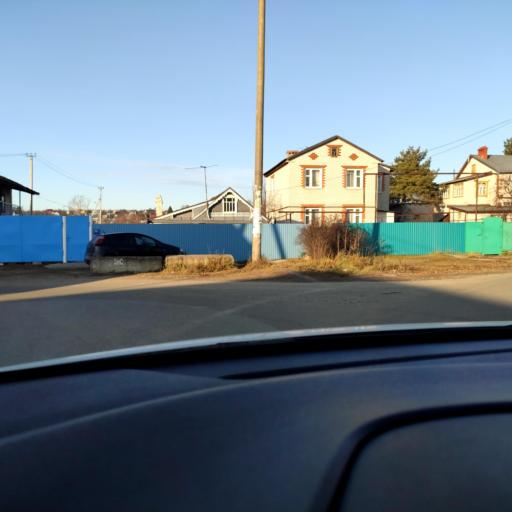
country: RU
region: Tatarstan
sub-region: Gorod Kazan'
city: Kazan
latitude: 55.8818
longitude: 49.0702
